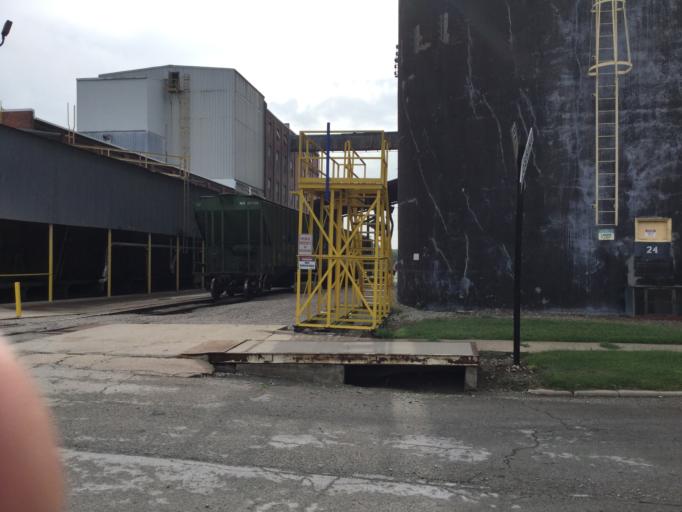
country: US
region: Kansas
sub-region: Montgomery County
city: Coffeyville
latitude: 37.0299
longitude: -95.6178
